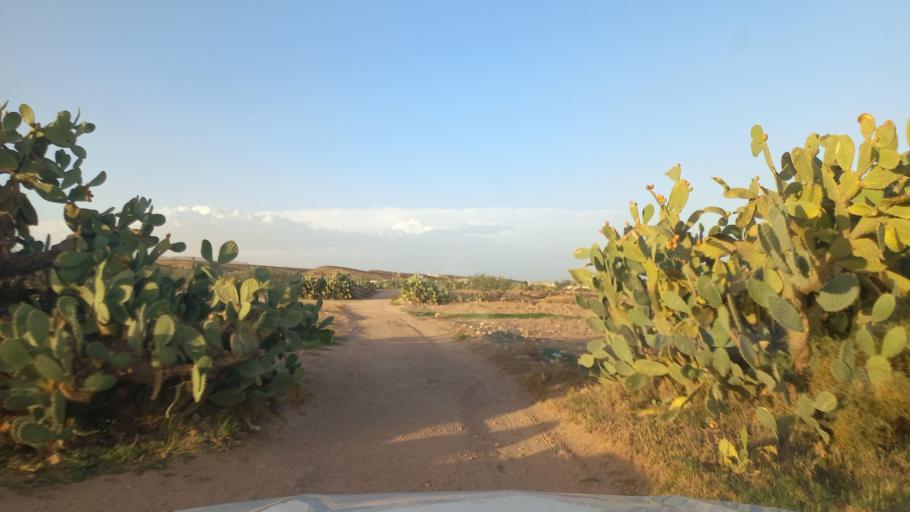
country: TN
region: Al Qasrayn
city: Sbiba
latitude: 35.3730
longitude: 9.0085
